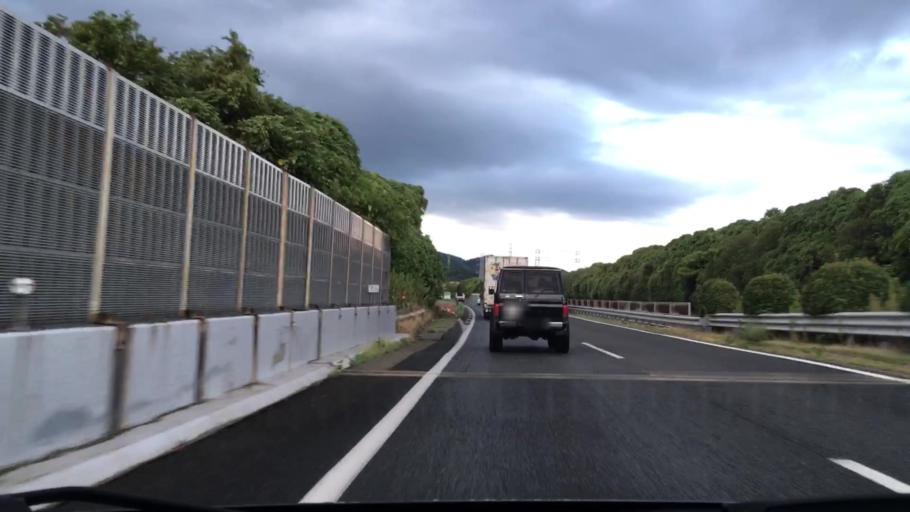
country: JP
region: Fukuoka
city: Kanda
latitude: 33.8409
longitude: 130.9272
